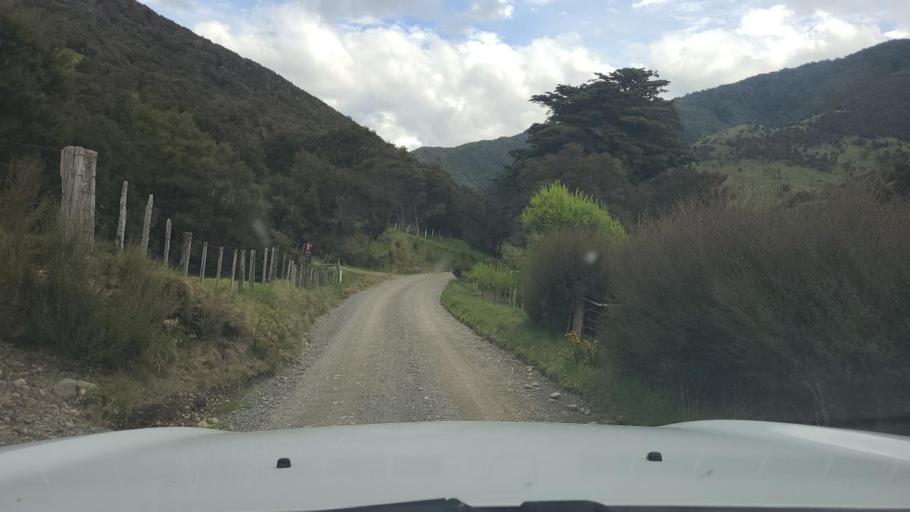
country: NZ
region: Wellington
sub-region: Masterton District
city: Masterton
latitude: -40.9335
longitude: 175.4802
